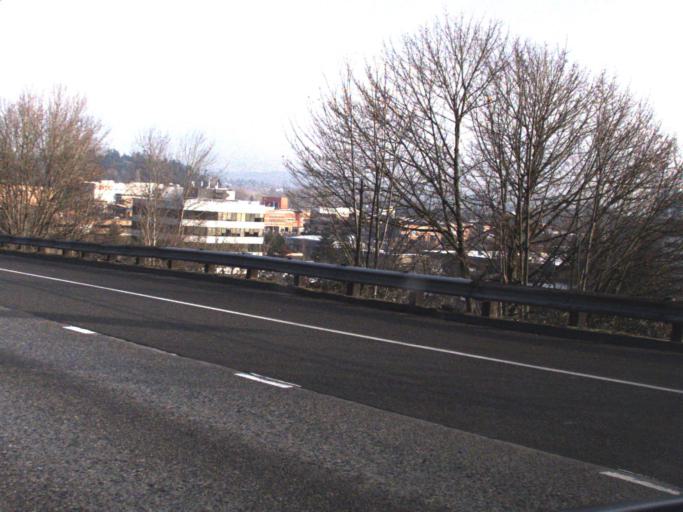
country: US
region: Washington
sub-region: King County
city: Tukwila
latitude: 47.4536
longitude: -122.2641
